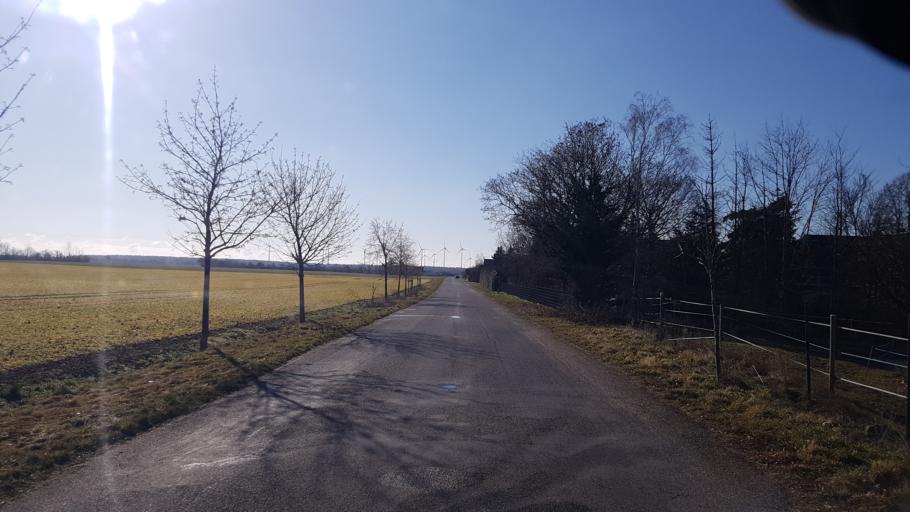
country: DE
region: Brandenburg
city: Muhlberg
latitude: 51.5035
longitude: 13.2315
